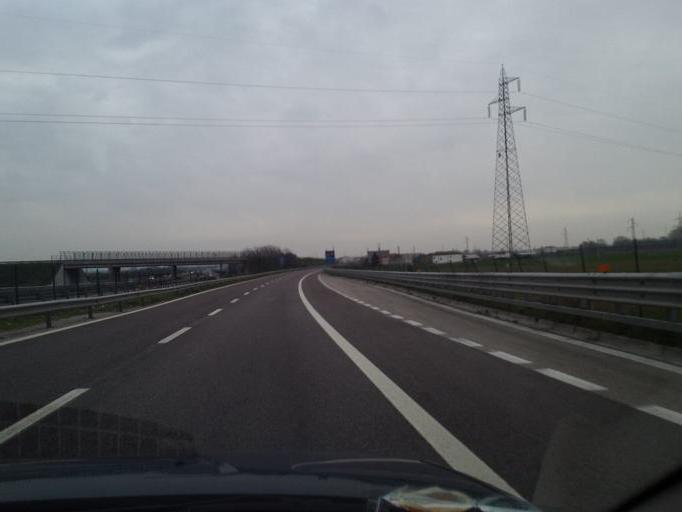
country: IT
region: Veneto
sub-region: Provincia di Verona
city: San Giovanni Lupatoto
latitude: 45.4023
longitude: 11.0356
